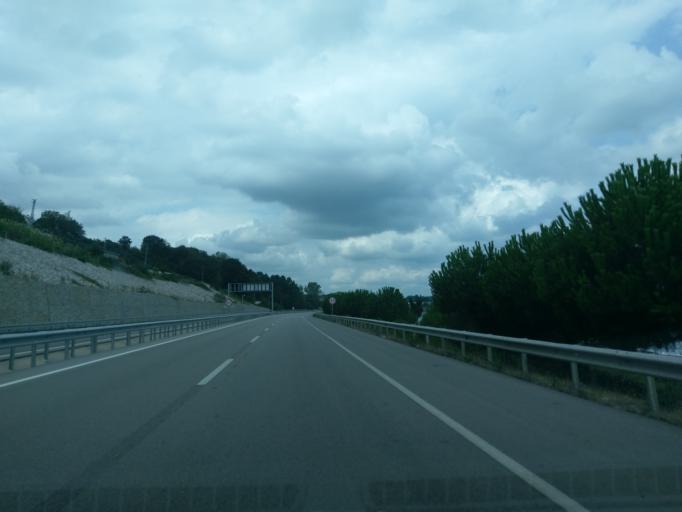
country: TR
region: Sinop
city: Gerze
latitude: 41.8287
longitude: 35.1622
